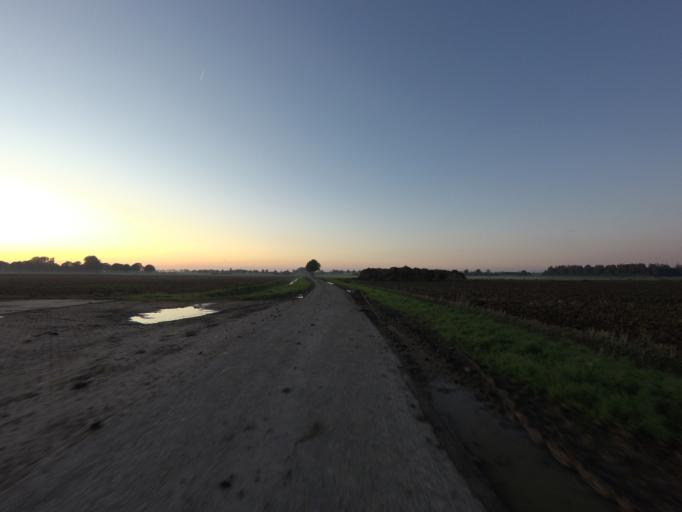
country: NL
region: North Brabant
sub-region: Gemeente Woudrichem
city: Almkerk
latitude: 51.7845
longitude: 4.9727
